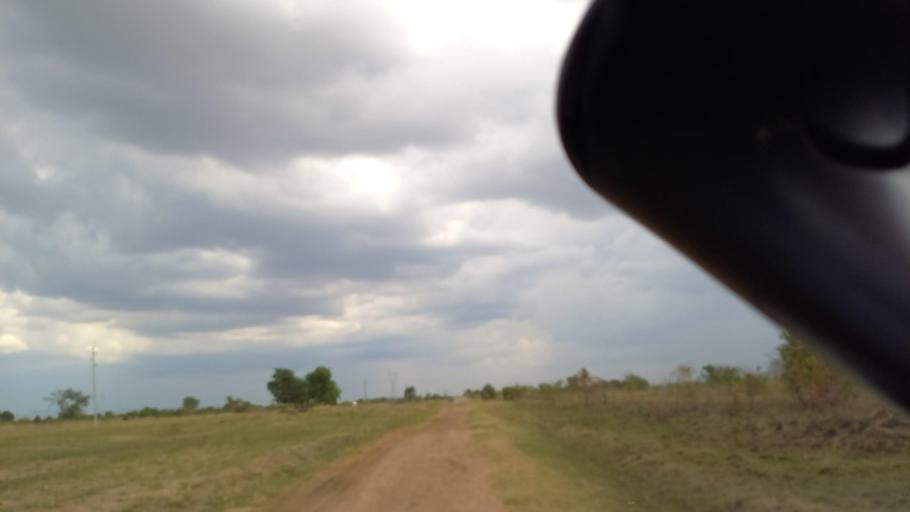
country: ZM
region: Lusaka
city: Kafue
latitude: -15.8455
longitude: 28.0980
